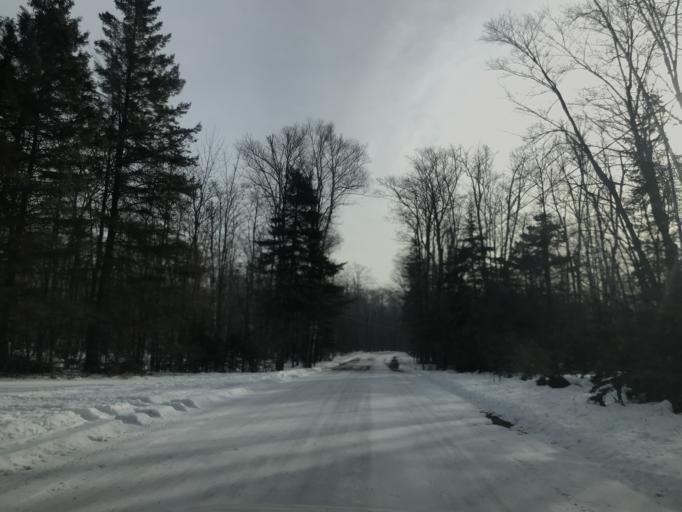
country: US
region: Wisconsin
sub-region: Door County
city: Sturgeon Bay
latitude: 45.1486
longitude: -87.0542
